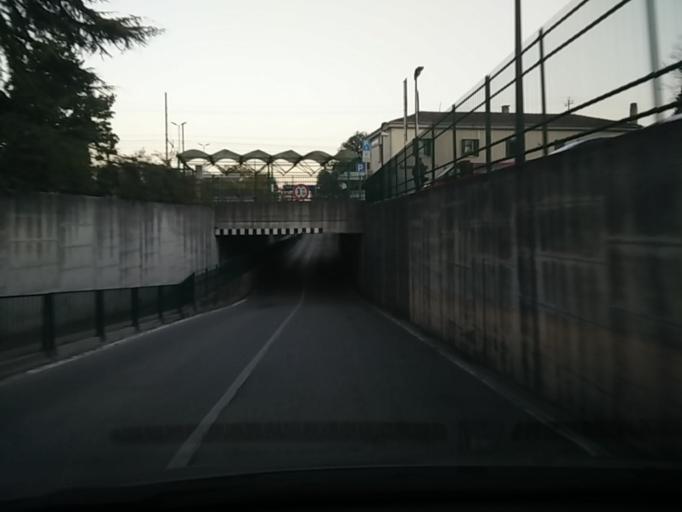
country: IT
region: Veneto
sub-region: Provincia di Treviso
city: Lancenigo-Villorba
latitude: 45.7104
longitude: 12.2651
